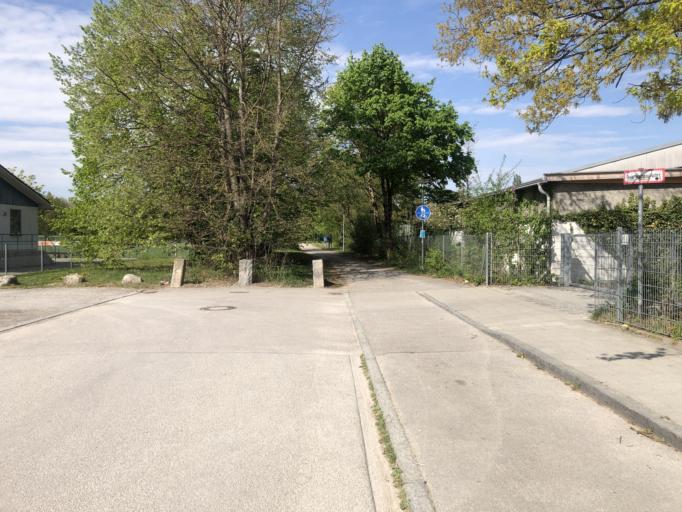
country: DE
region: Bavaria
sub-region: Upper Bavaria
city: Bogenhausen
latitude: 48.1205
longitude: 11.6377
